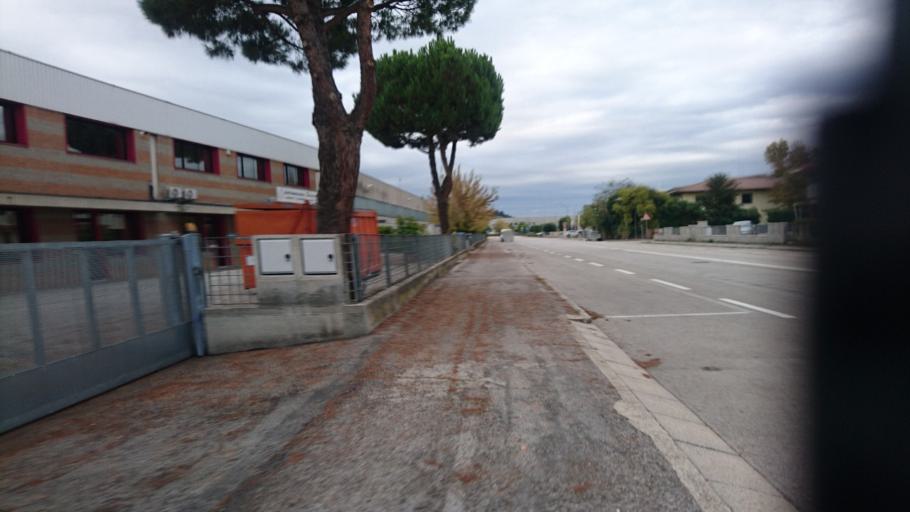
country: IT
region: Veneto
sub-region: Provincia di Vicenza
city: Sovizzo
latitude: 45.5253
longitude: 11.4514
